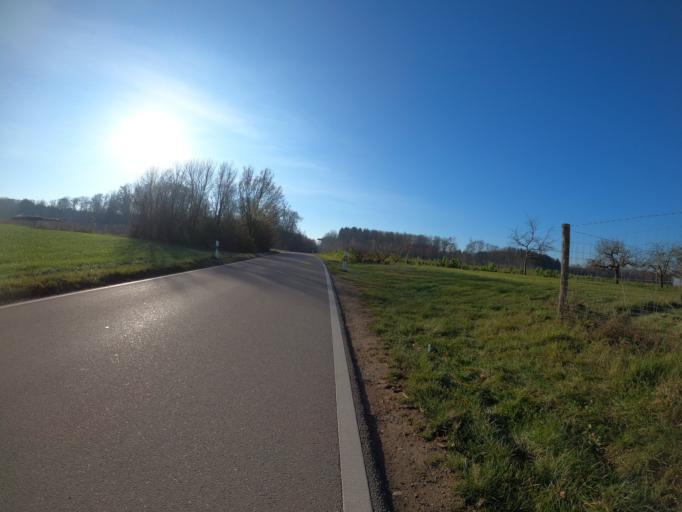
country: DE
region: Baden-Wuerttemberg
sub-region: Regierungsbezirk Stuttgart
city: Ebersbach an der Fils
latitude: 48.7025
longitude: 9.5413
